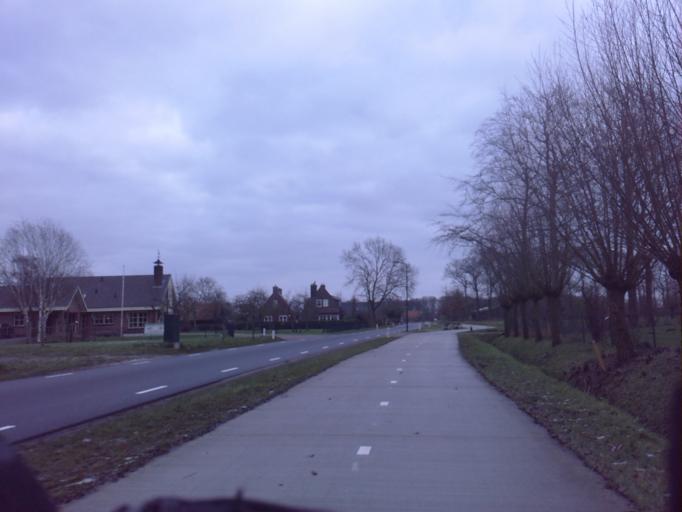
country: NL
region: Utrecht
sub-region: Gemeente Leusden
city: Leusden
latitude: 52.1315
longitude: 5.4553
